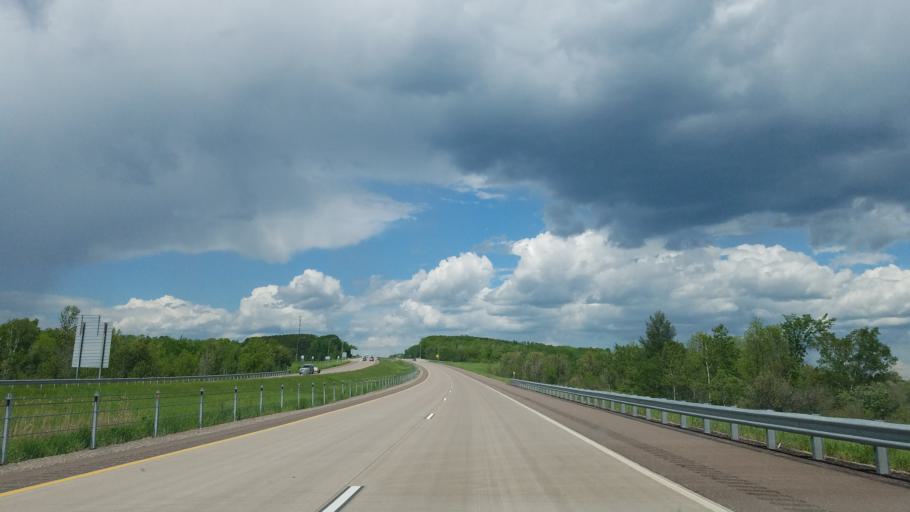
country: US
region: Minnesota
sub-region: Carlton County
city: Moose Lake
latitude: 46.4491
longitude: -92.7333
